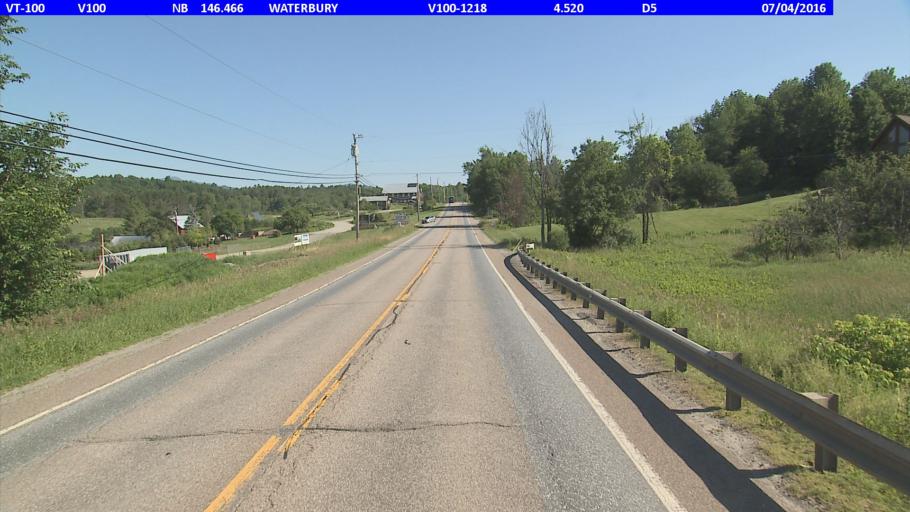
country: US
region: Vermont
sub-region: Washington County
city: Waterbury
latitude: 44.3943
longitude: -72.7192
